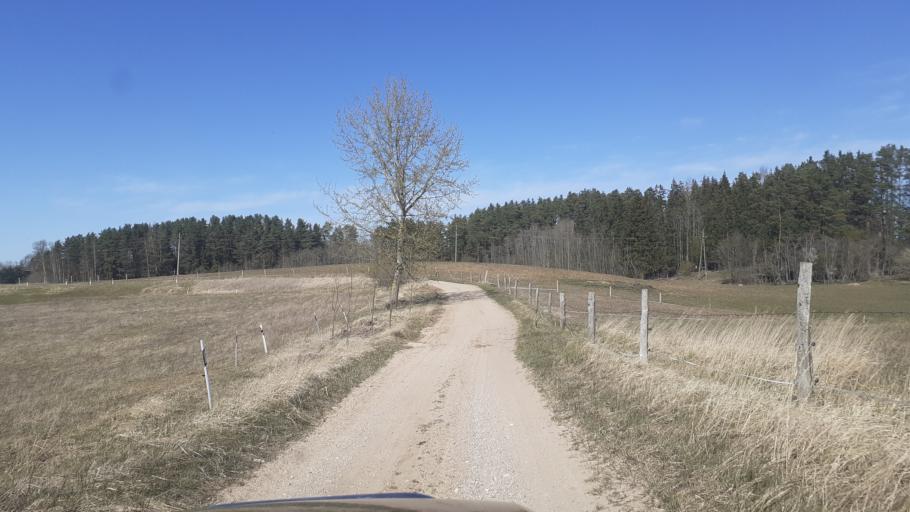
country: LV
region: Kuldigas Rajons
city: Kuldiga
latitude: 56.8345
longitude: 22.0076
